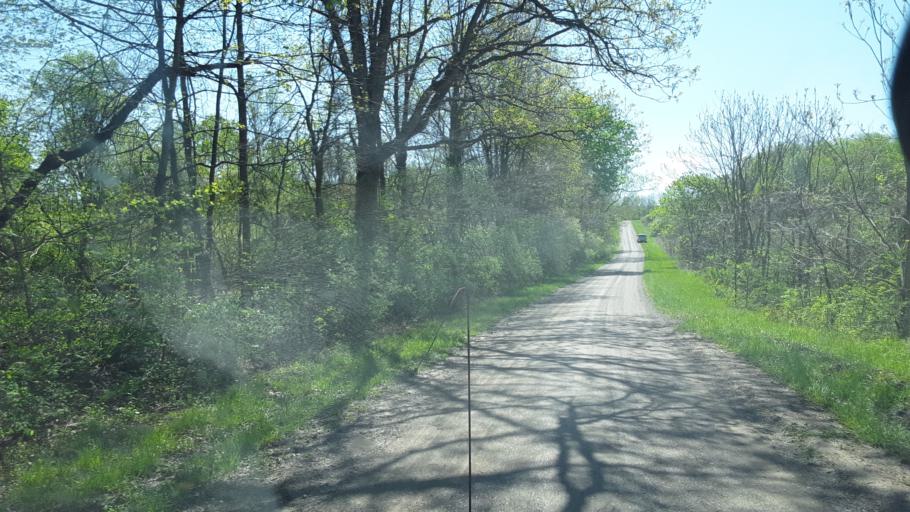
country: US
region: Ohio
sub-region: Noble County
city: Caldwell
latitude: 39.7836
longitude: -81.6241
